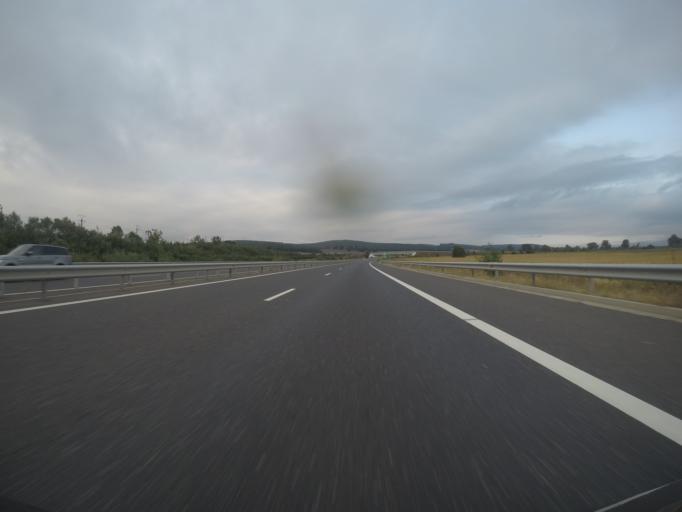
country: RO
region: Hunedoara
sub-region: Comuna Turdas
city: Turdas
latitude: 45.8431
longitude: 23.1253
